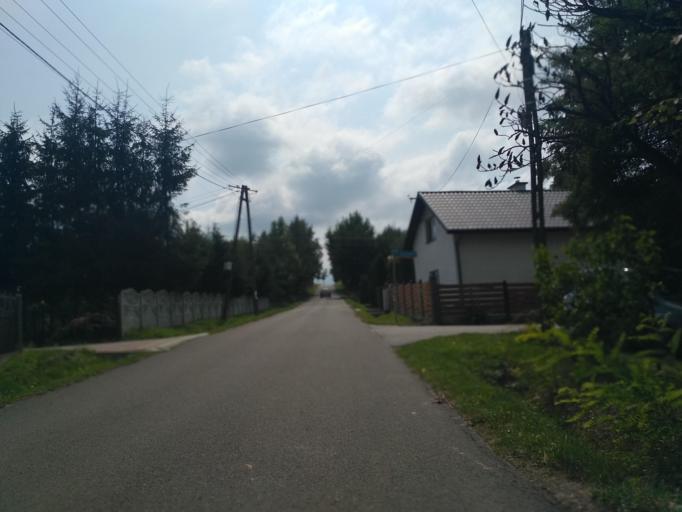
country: PL
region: Subcarpathian Voivodeship
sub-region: Powiat lancucki
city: Kraczkowa
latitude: 50.0083
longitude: 22.1507
